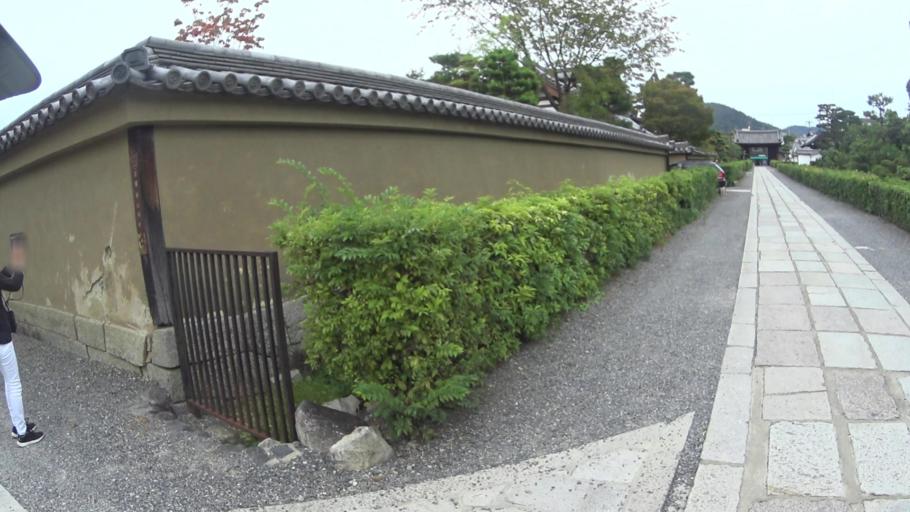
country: JP
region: Kyoto
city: Kyoto
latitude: 35.0248
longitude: 135.7199
